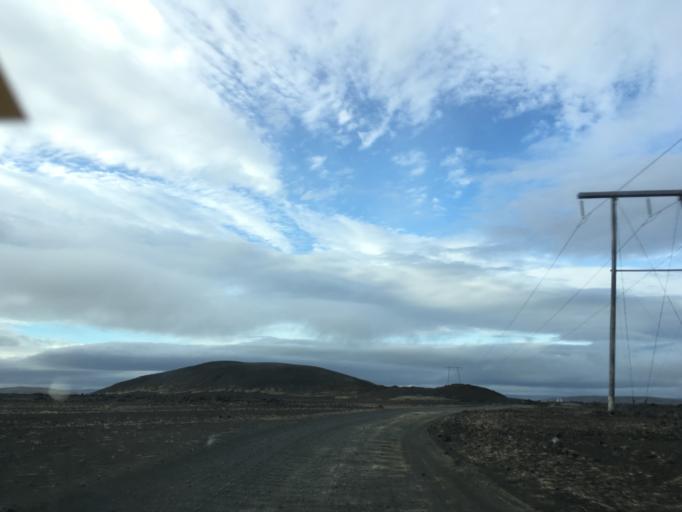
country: IS
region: South
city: Vestmannaeyjar
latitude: 64.1228
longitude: -19.1183
